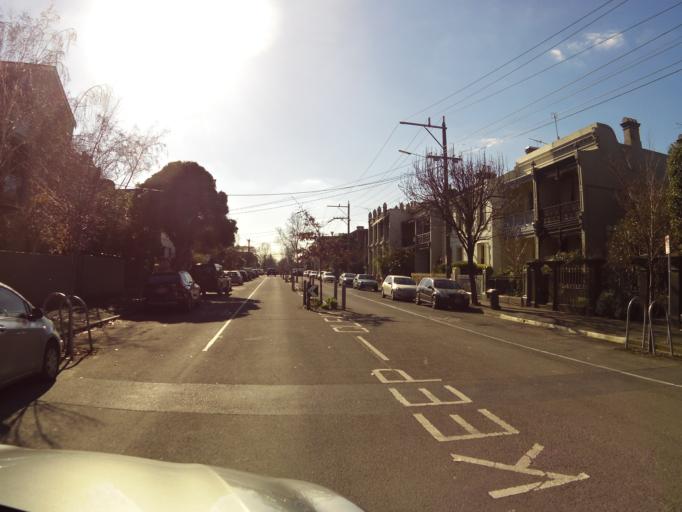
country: AU
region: Victoria
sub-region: Yarra
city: Collingwood
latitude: -37.8076
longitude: 144.9803
